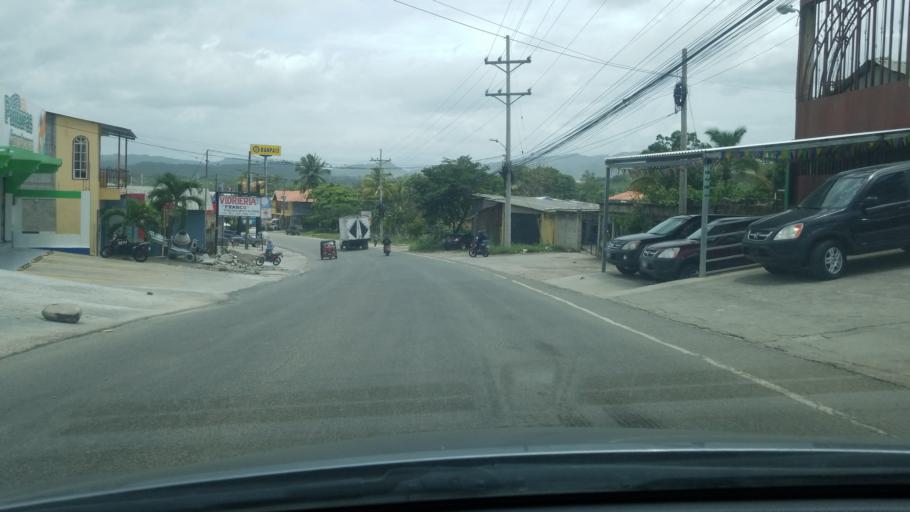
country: HN
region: Copan
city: Cucuyagua
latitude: 14.6554
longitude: -88.8747
